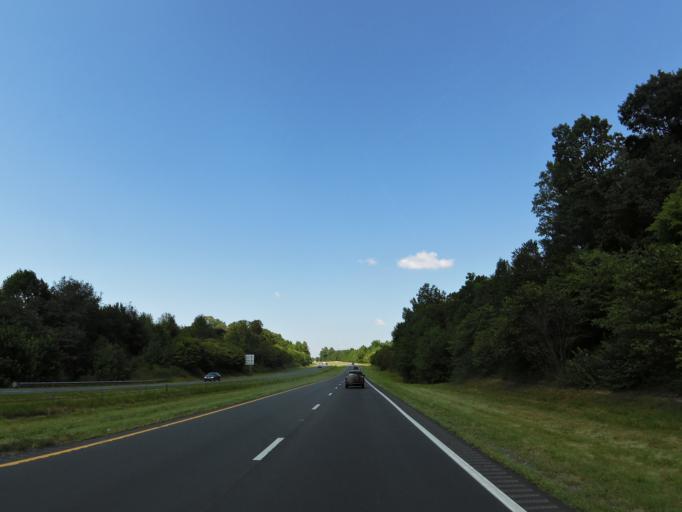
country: US
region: North Carolina
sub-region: Lincoln County
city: Lincolnton
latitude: 35.4952
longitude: -81.2282
